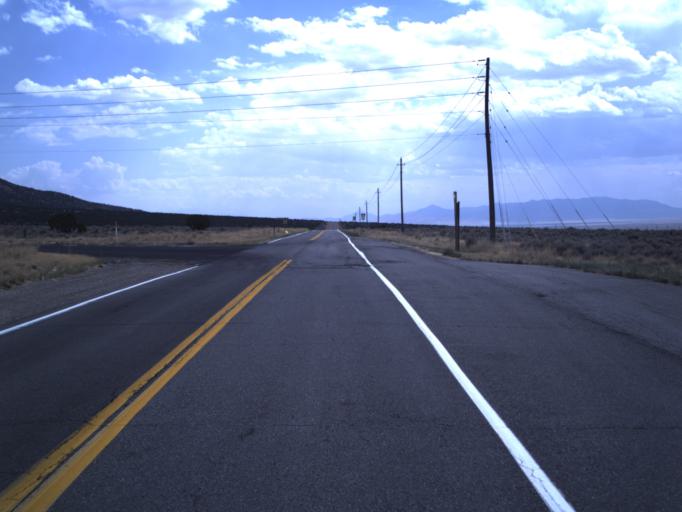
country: US
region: Utah
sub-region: Tooele County
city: Tooele
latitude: 40.3511
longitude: -112.3105
